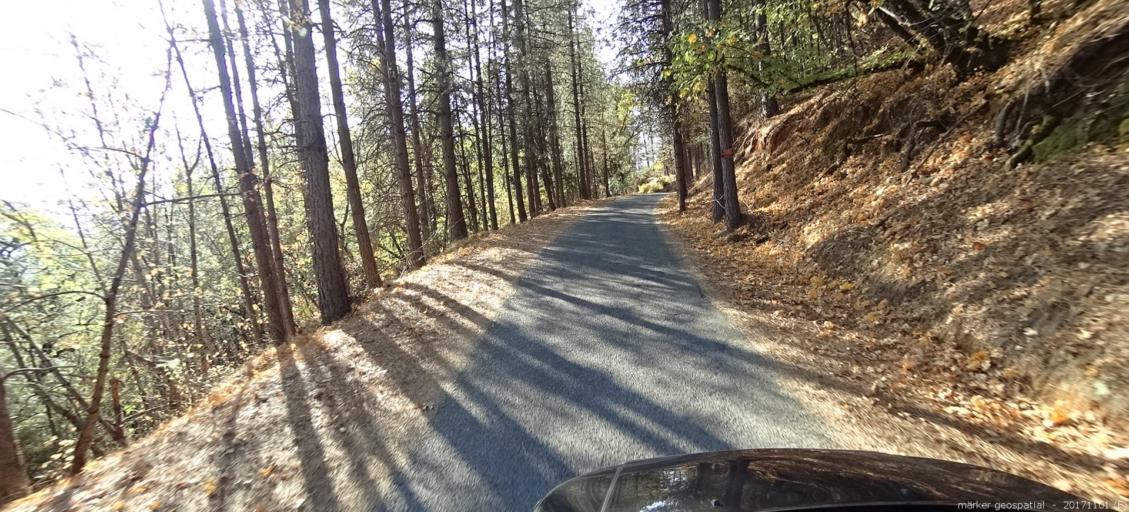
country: US
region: California
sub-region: Shasta County
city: Shasta Lake
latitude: 40.8111
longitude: -122.3107
